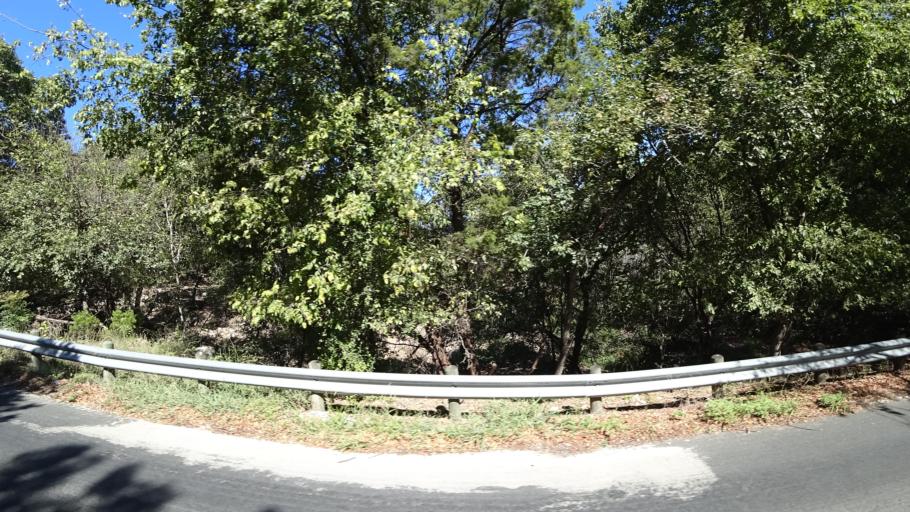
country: US
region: Texas
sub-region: Travis County
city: West Lake Hills
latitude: 30.3101
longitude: -97.7995
